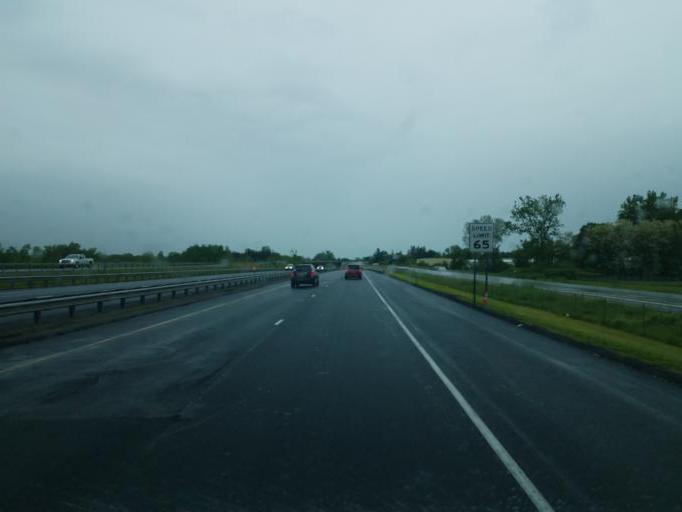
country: US
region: New York
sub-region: Oneida County
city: Yorkville
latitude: 43.1338
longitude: -75.2644
